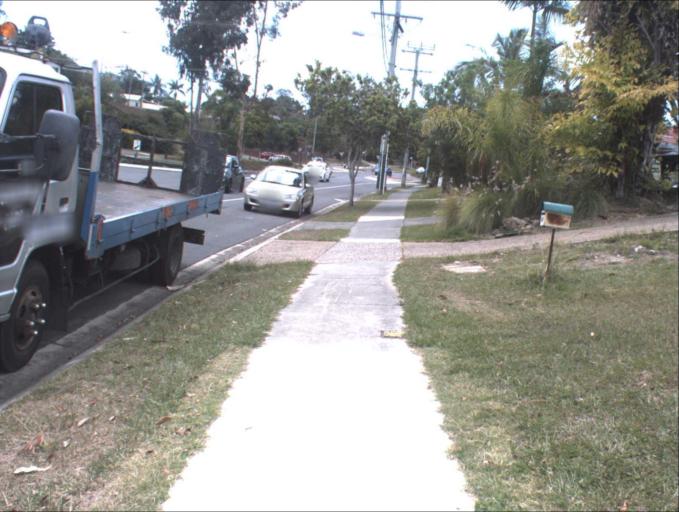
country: AU
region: Queensland
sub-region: Logan
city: Slacks Creek
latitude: -27.6535
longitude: 153.1726
